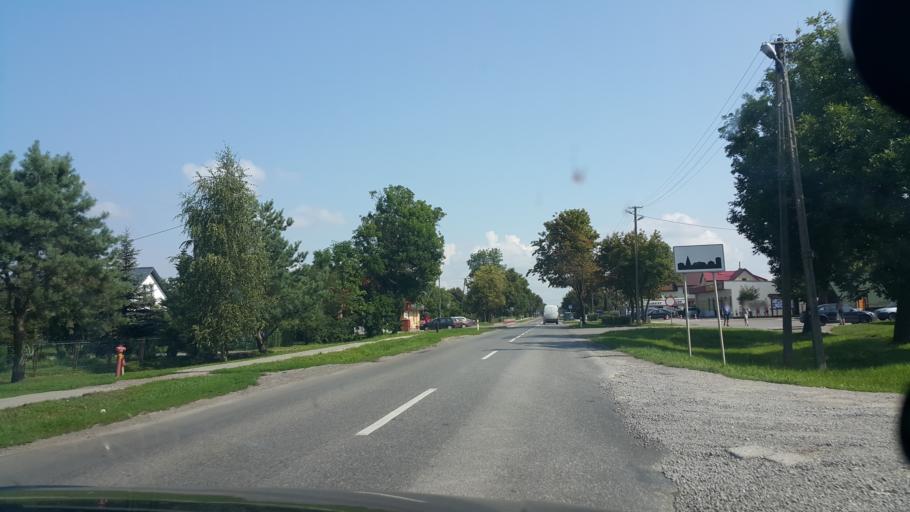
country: PL
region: Lublin Voivodeship
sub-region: Powiat wlodawski
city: Urszulin
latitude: 51.3909
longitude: 23.1931
